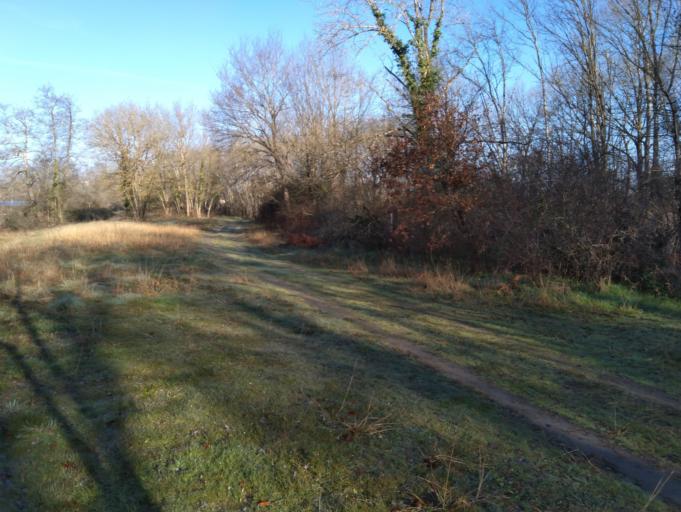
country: FR
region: Midi-Pyrenees
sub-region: Departement du Gers
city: Riscle
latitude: 43.6622
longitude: -0.0784
